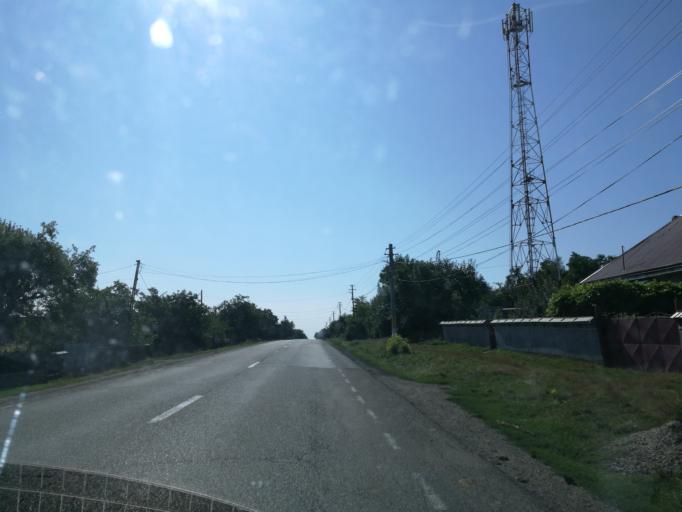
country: RO
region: Suceava
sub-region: Comuna Draguseni
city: Draguseni
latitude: 47.2845
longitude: 26.5024
